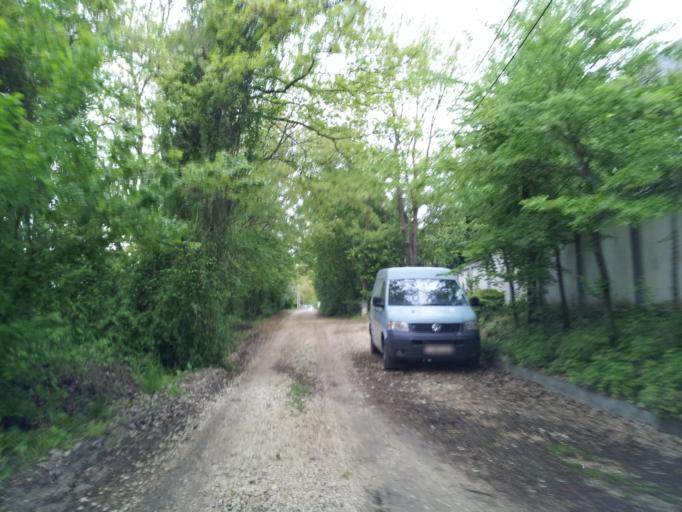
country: HU
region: Pest
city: Erd
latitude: 47.4050
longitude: 18.9246
